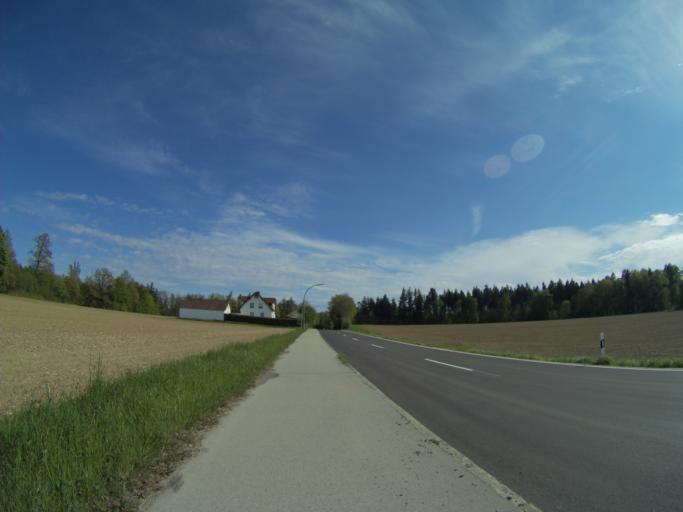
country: DE
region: Bavaria
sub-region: Upper Bavaria
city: Freising
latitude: 48.4231
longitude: 11.7335
